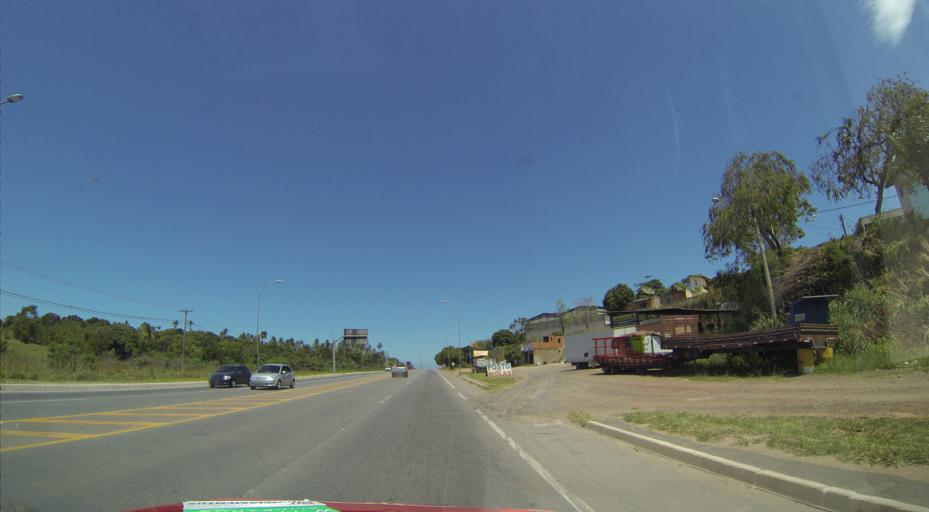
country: BR
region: Espirito Santo
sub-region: Serra
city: Serra
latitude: -20.1262
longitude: -40.3016
